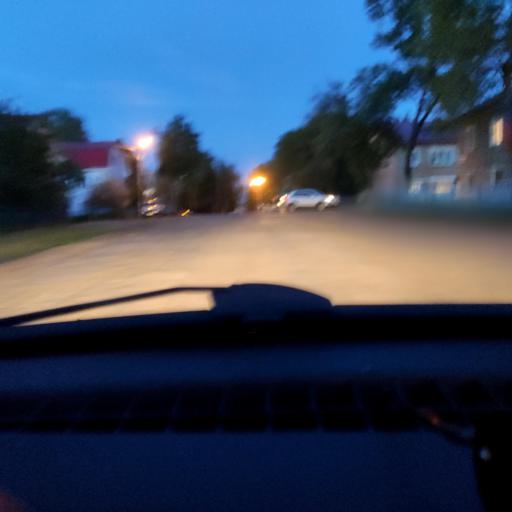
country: RU
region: Bashkortostan
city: Karmaskaly
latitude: 54.3699
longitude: 56.1683
